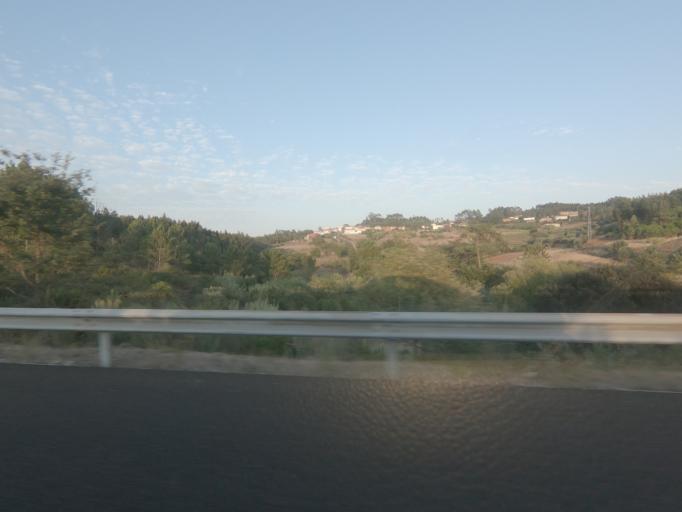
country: PT
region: Leiria
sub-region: Leiria
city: Caranguejeira
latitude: 39.7727
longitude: -8.7438
